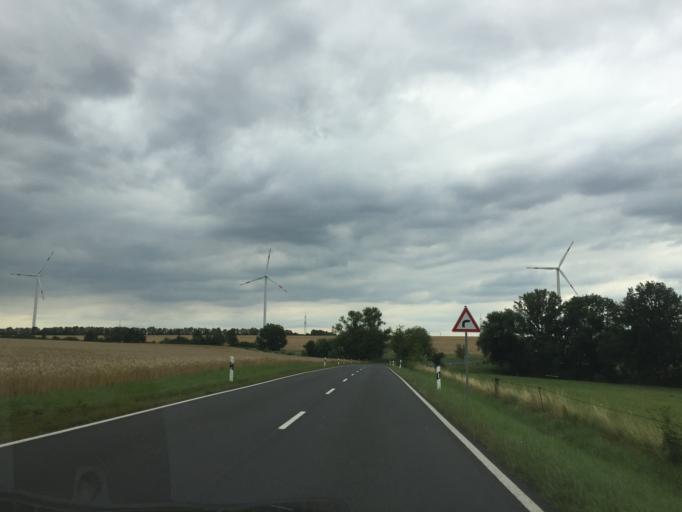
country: DE
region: Thuringia
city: Schmolln
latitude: 50.8761
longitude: 12.3795
